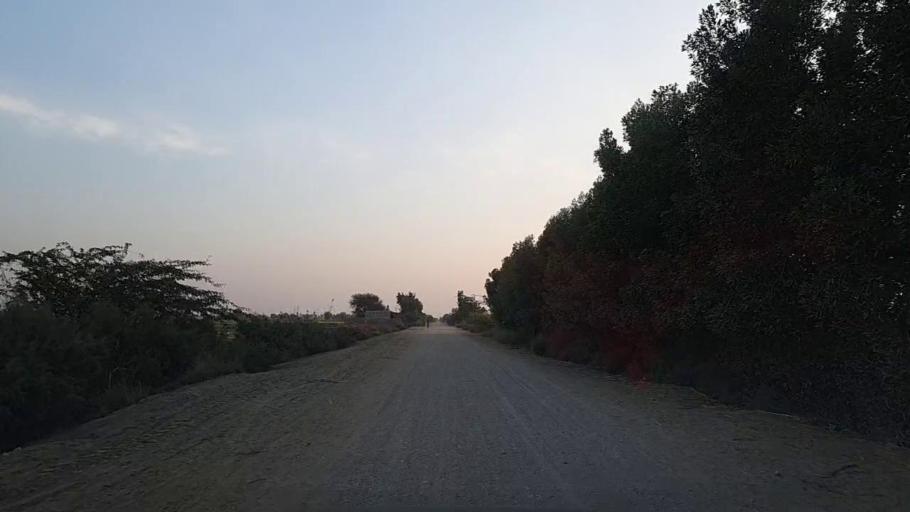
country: PK
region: Sindh
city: Tando Mittha Khan
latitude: 25.9723
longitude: 69.1105
